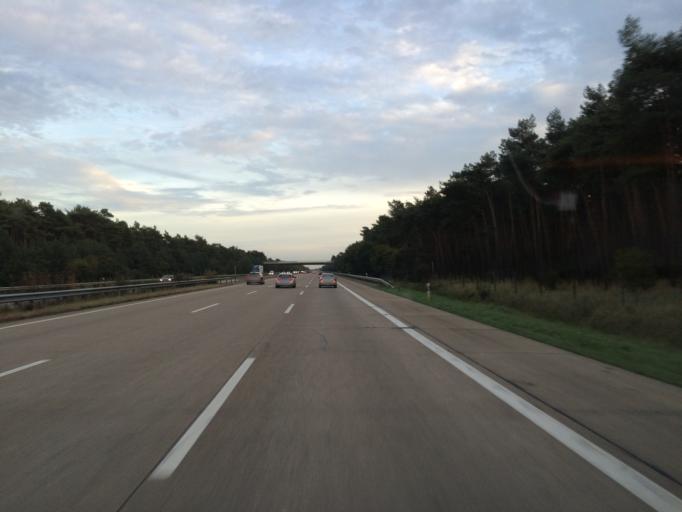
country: DE
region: Lower Saxony
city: Lindwedel
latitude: 52.6324
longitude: 9.7200
